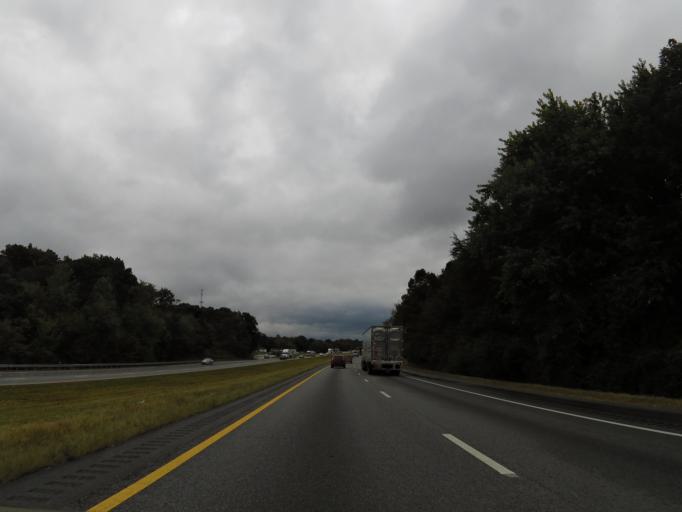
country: US
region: Georgia
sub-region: Walker County
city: Lookout Mountain
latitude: 34.9967
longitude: -85.3984
